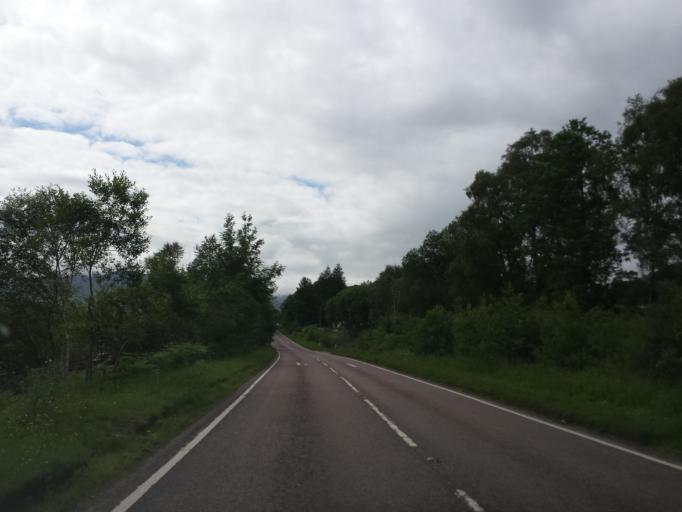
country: GB
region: Scotland
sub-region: Highland
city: Fort William
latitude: 56.8548
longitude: -5.2536
